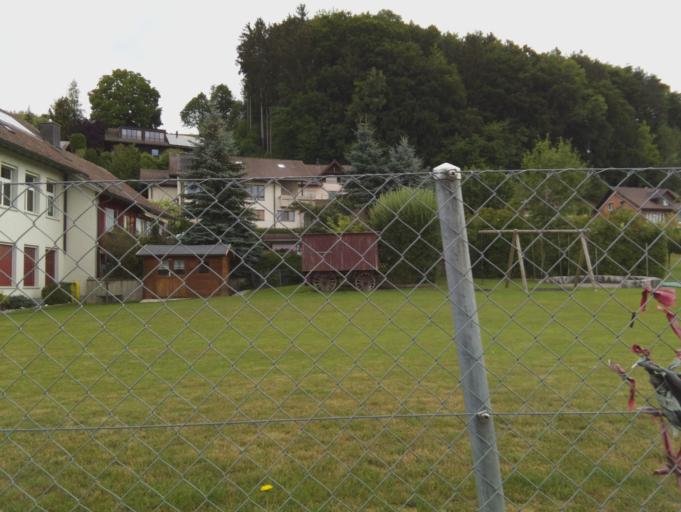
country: CH
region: Saint Gallen
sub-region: Wahlkreis Toggenburg
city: Lutisburg
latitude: 47.3990
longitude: 9.0821
